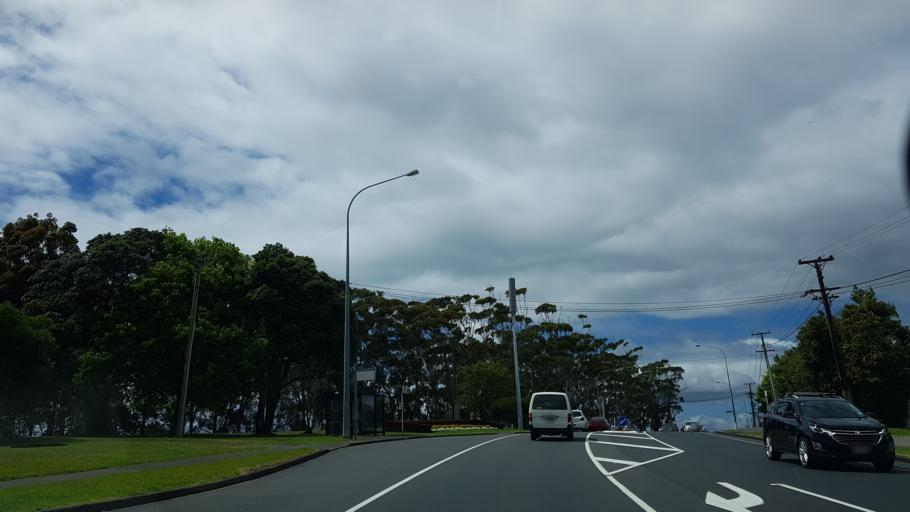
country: NZ
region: Auckland
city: Murrays Bay
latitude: -36.7476
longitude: 174.7459
